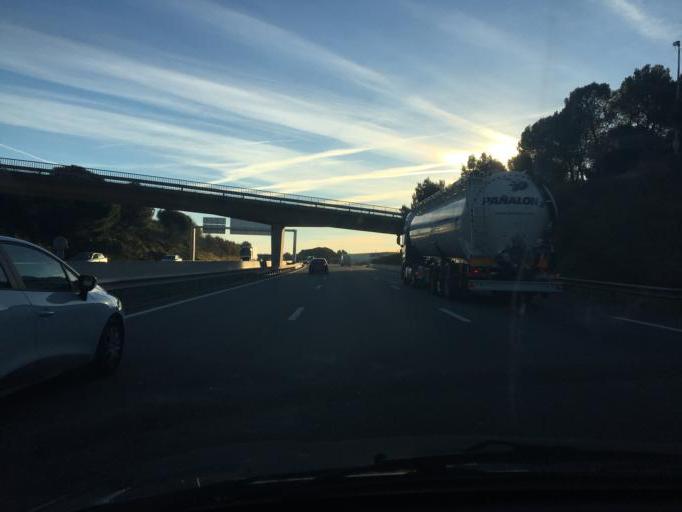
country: FR
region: Provence-Alpes-Cote d'Azur
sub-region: Departement du Var
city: Puget-sur-Argens
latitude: 43.4592
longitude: 6.6882
